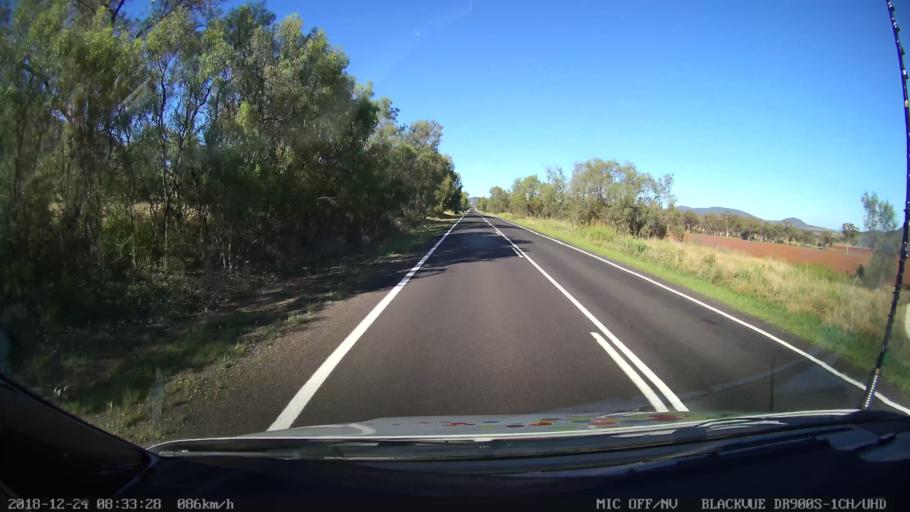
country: AU
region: New South Wales
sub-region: Liverpool Plains
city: Quirindi
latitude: -31.2865
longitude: 150.6841
